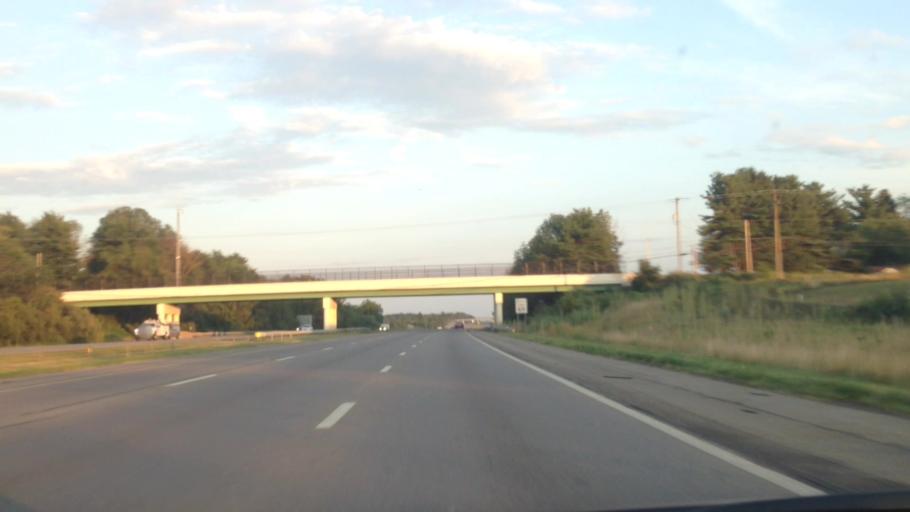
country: US
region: Ohio
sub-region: Summit County
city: Greensburg
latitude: 40.9562
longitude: -81.4567
